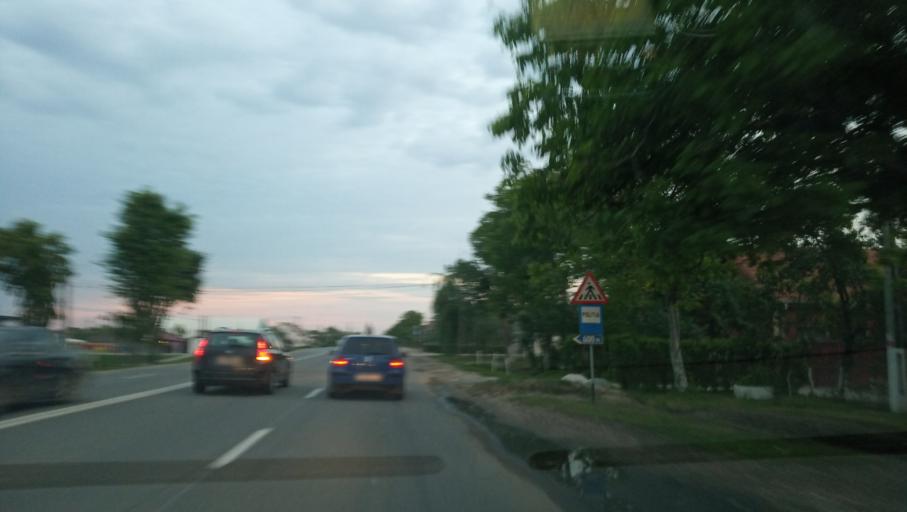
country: RO
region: Timis
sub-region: Comuna Sag
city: Sag
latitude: 45.6505
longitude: 21.1746
